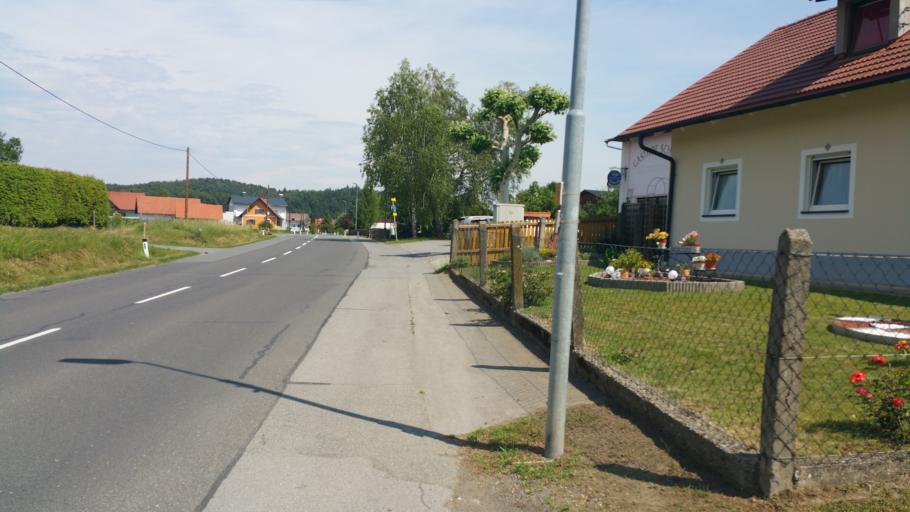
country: AT
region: Styria
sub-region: Politischer Bezirk Leibnitz
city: Pistorf
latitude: 46.7638
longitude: 15.3734
